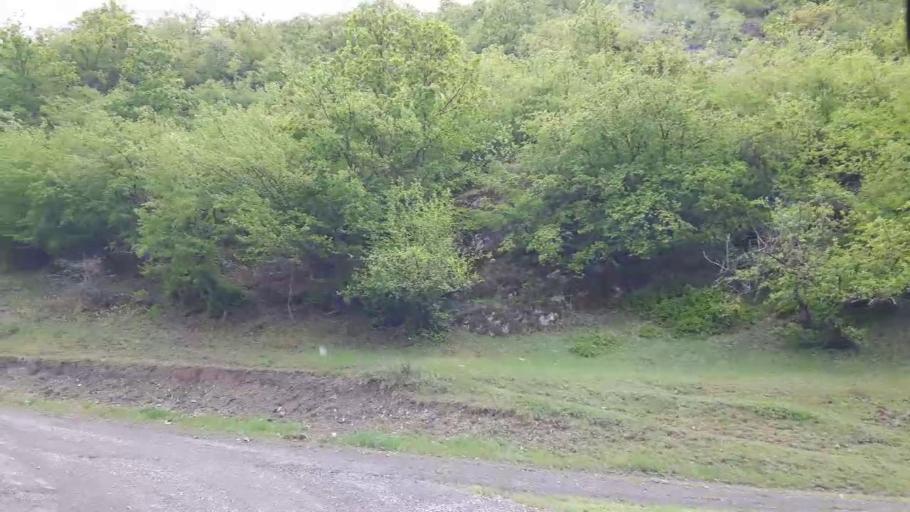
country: GE
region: Shida Kartli
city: Gori
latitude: 41.8905
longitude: 44.0056
